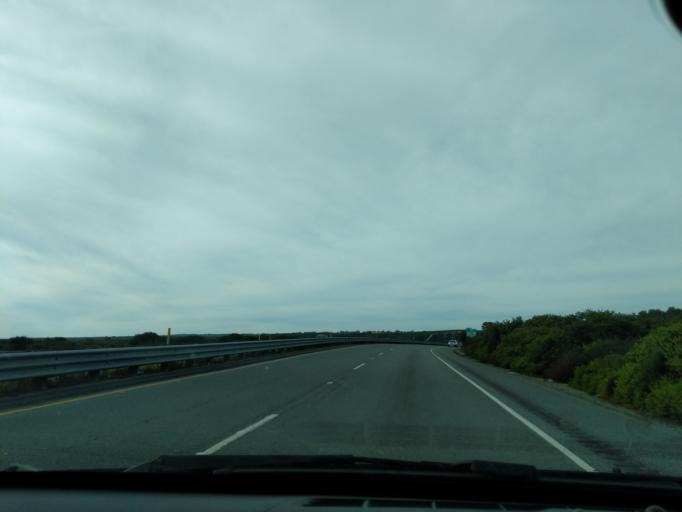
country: US
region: California
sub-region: Santa Barbara County
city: Vandenberg Village
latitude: 34.7067
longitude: -120.4844
